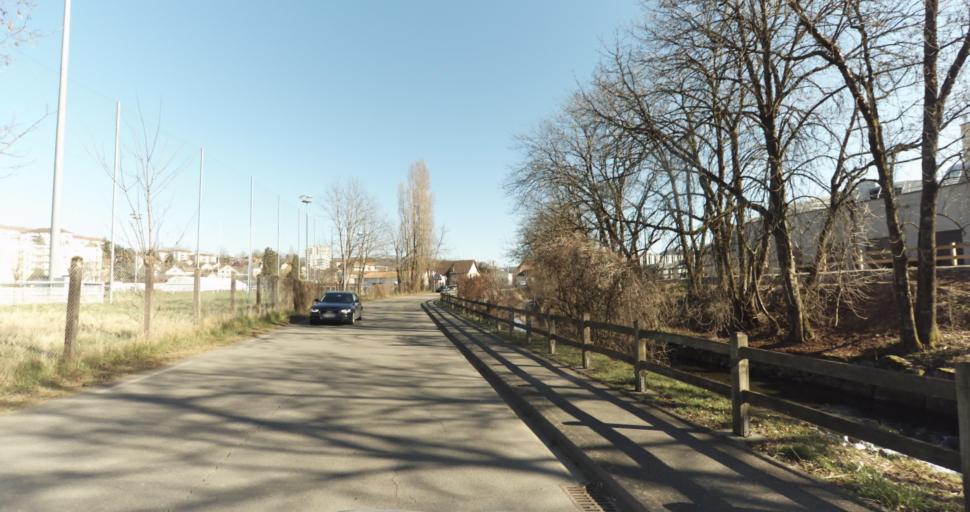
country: FR
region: Franche-Comte
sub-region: Departement du Jura
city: Lons-le-Saunier
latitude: 46.6765
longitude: 5.5394
